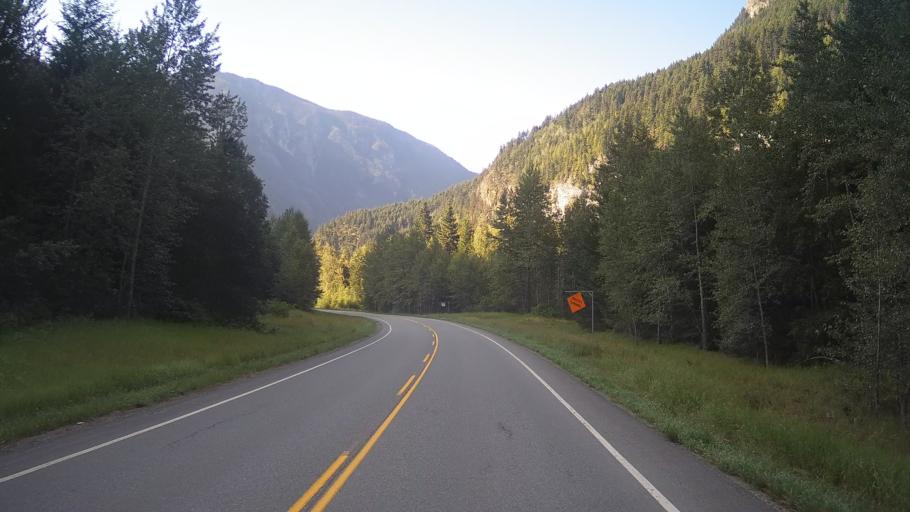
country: CA
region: British Columbia
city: Lillooet
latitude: 50.5870
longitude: -122.0939
